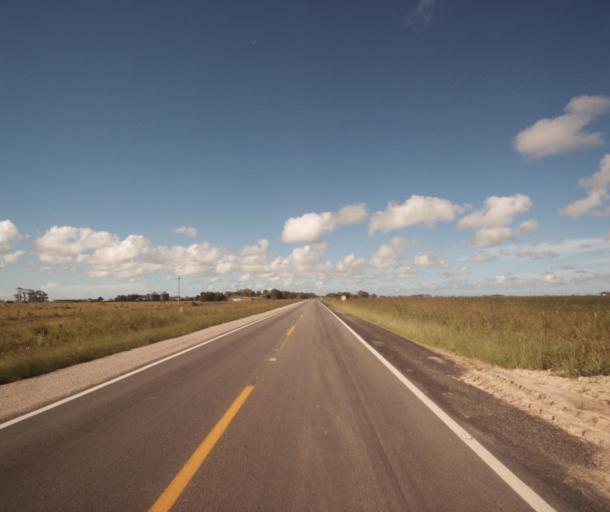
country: UY
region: Cerro Largo
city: Rio Branco
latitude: -33.0396
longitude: -52.8613
